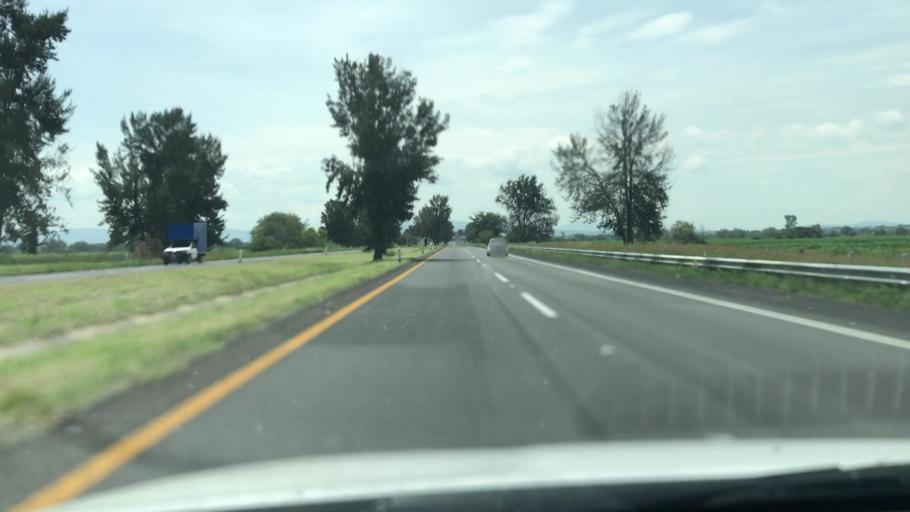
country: MX
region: Michoacan
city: Vistahermosa de Negrete
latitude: 20.2994
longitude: -102.4818
